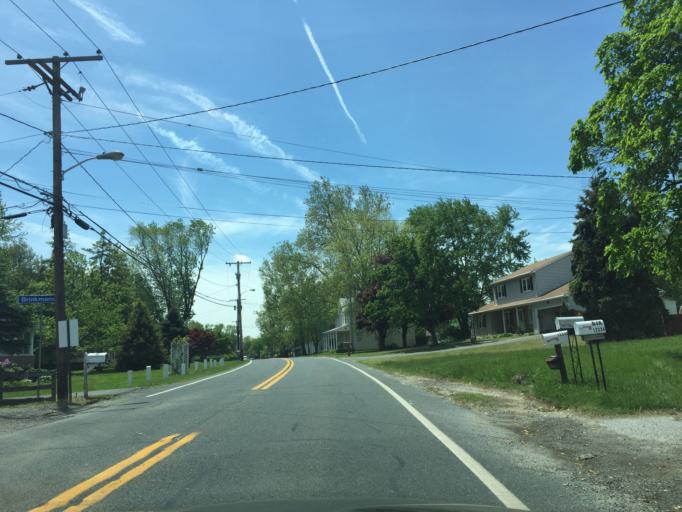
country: US
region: Maryland
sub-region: Baltimore County
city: Bowleys Quarters
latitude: 39.3580
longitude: -76.3723
